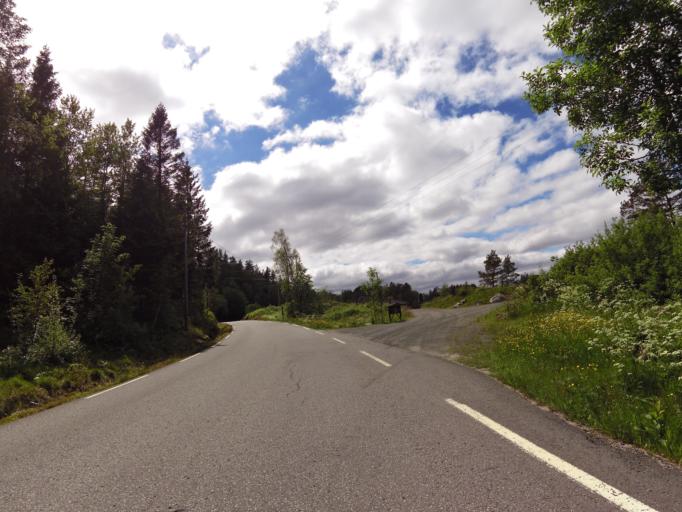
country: NO
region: Vest-Agder
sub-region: Kvinesdal
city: Liknes
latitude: 58.2843
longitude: 6.9294
